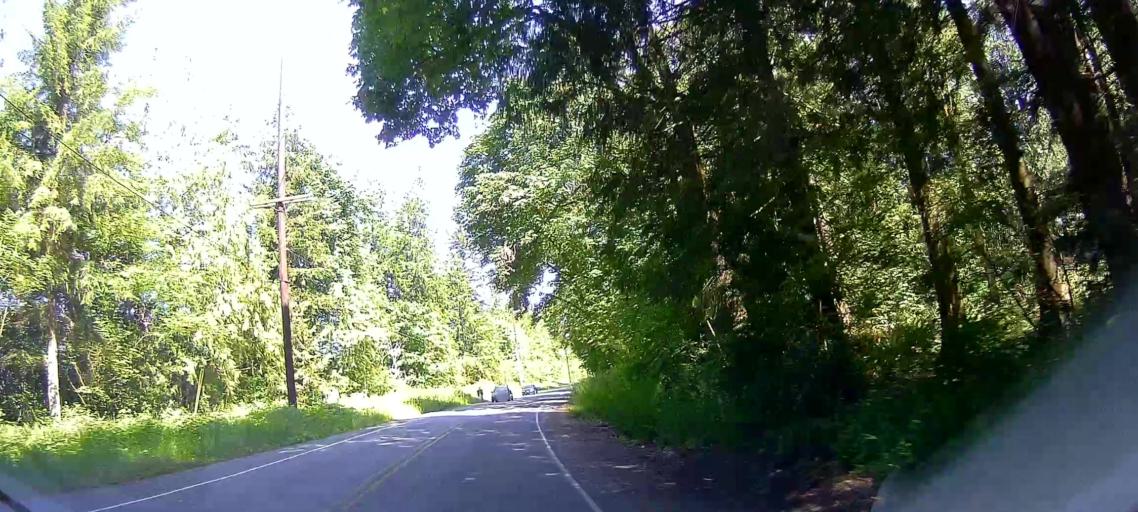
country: US
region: Washington
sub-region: Skagit County
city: Burlington
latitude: 48.5352
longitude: -122.3095
